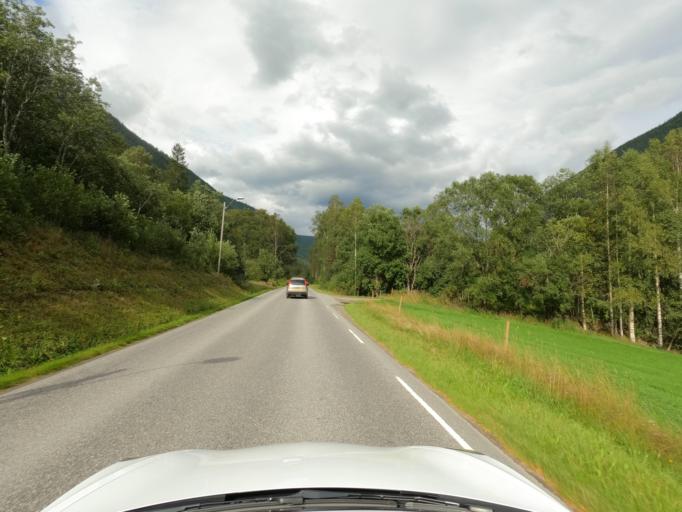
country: NO
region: Telemark
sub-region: Tinn
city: Rjukan
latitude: 59.8996
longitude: 8.7046
